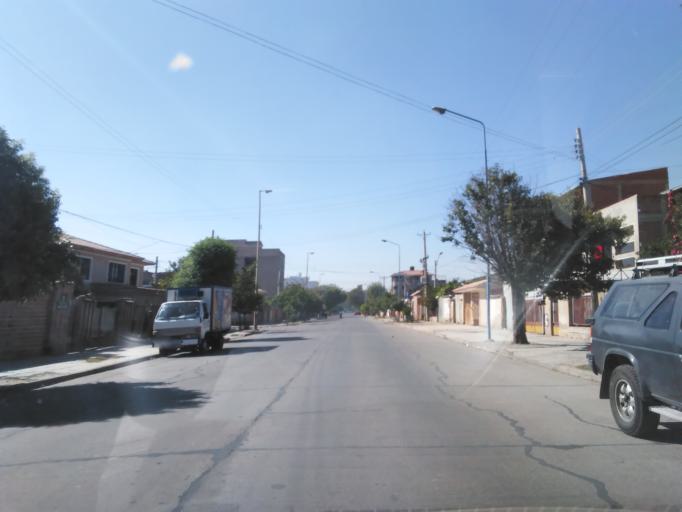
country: BO
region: Cochabamba
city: Cochabamba
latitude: -17.3997
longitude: -66.1817
